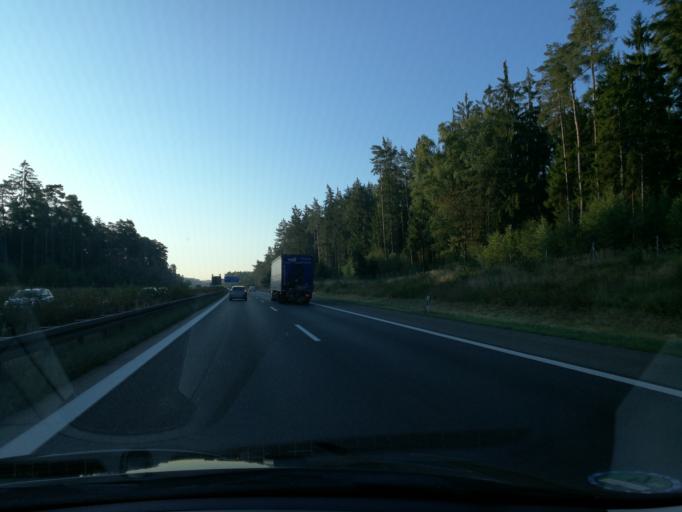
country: DE
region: Bavaria
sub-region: Regierungsbezirk Mittelfranken
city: Winkelhaid
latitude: 49.4145
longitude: 11.2852
